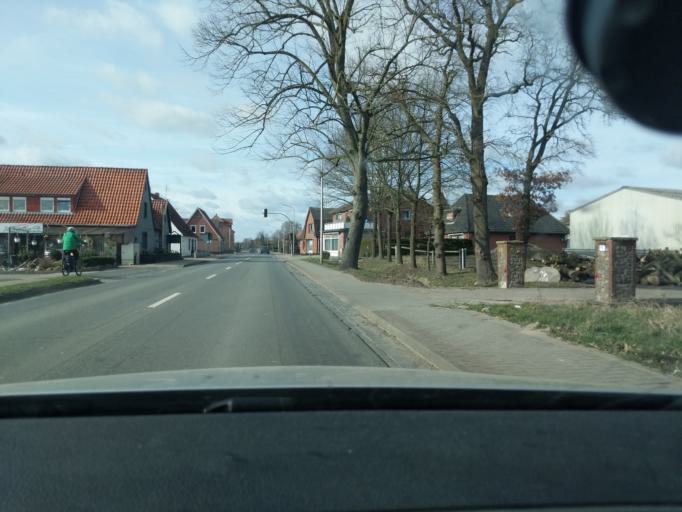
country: DE
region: Lower Saxony
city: Drochtersen
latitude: 53.6923
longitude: 9.4325
